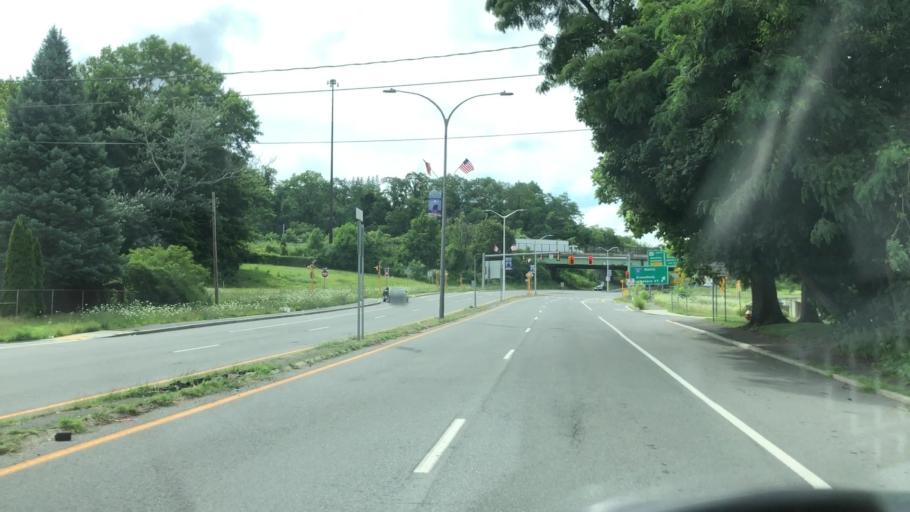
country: US
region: Massachusetts
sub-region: Hampden County
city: Holyoke
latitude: 42.1991
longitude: -72.6359
